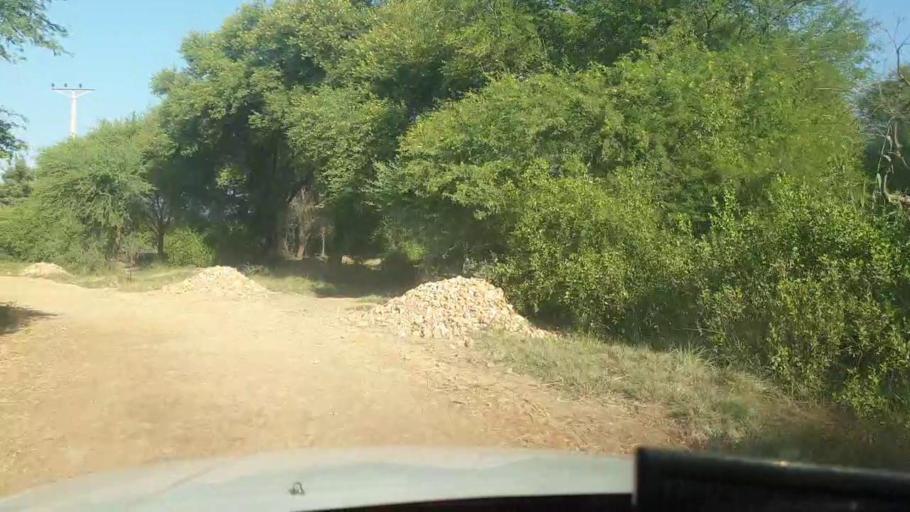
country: PK
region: Sindh
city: Mirpur Sakro
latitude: 24.5007
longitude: 67.6245
